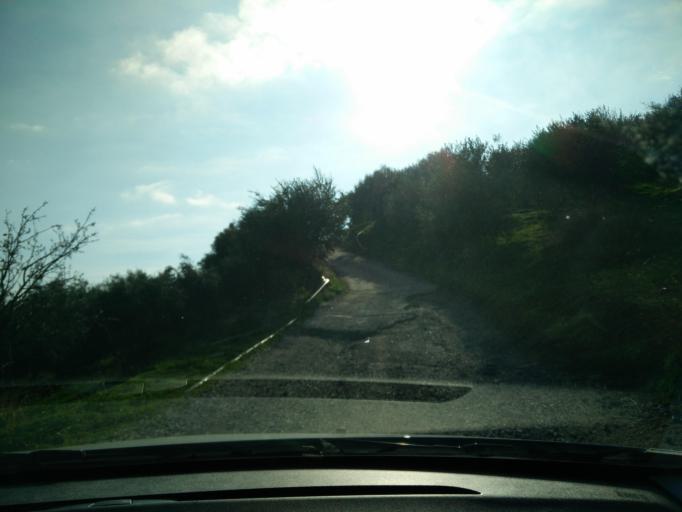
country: GR
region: Crete
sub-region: Nomos Lasithiou
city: Gra Liyia
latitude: 35.0295
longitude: 25.5669
